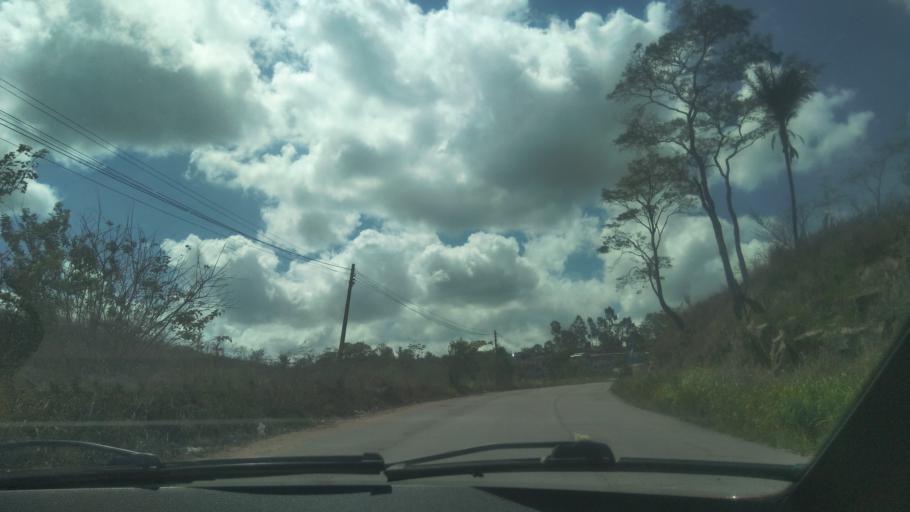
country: BR
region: Pernambuco
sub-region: Vitoria De Santo Antao
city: Vitoria de Santo Antao
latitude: -8.1356
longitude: -35.2764
